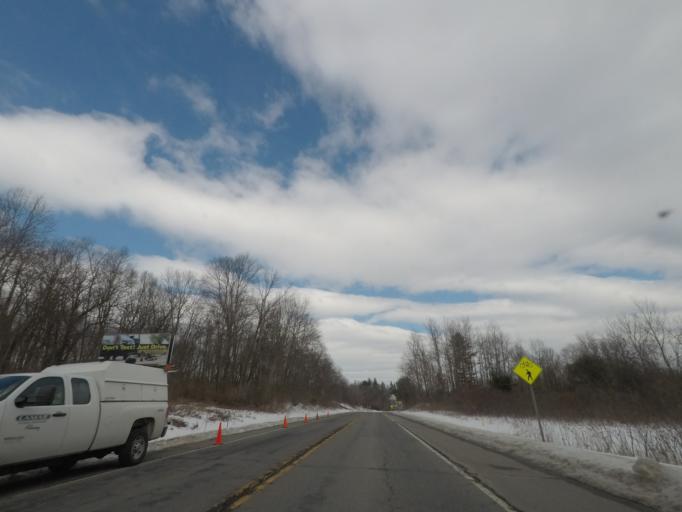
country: US
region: New York
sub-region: Saratoga County
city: Schuylerville
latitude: 43.0927
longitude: -73.5832
